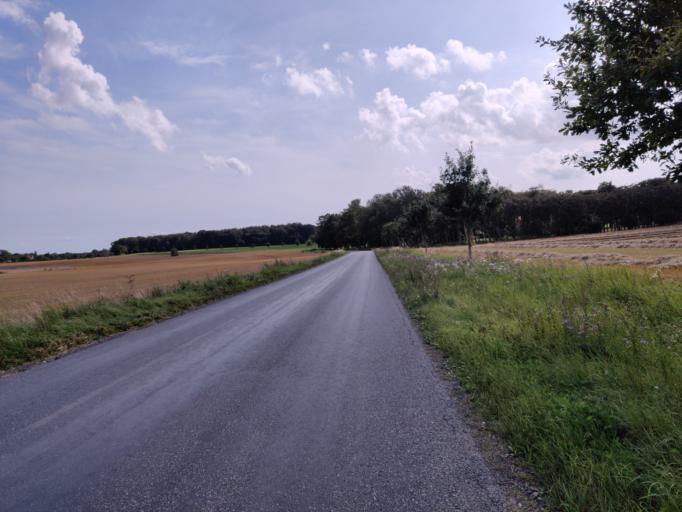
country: DK
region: Zealand
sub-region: Guldborgsund Kommune
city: Nykobing Falster
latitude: 54.6507
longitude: 11.8876
